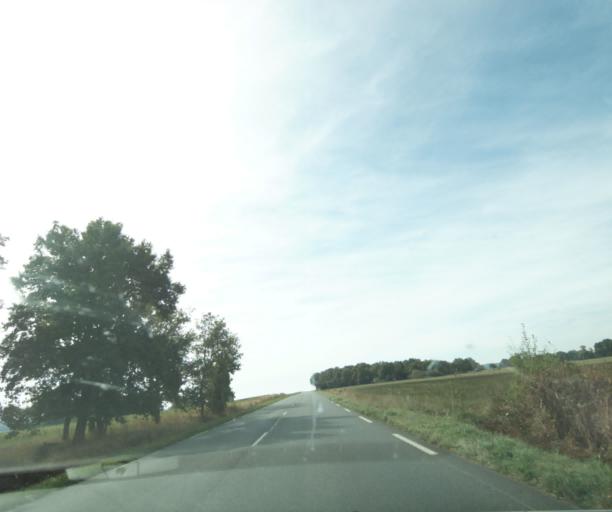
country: FR
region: Auvergne
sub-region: Departement de l'Allier
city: Saint-Gerand-le-Puy
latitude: 46.1999
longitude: 3.4968
